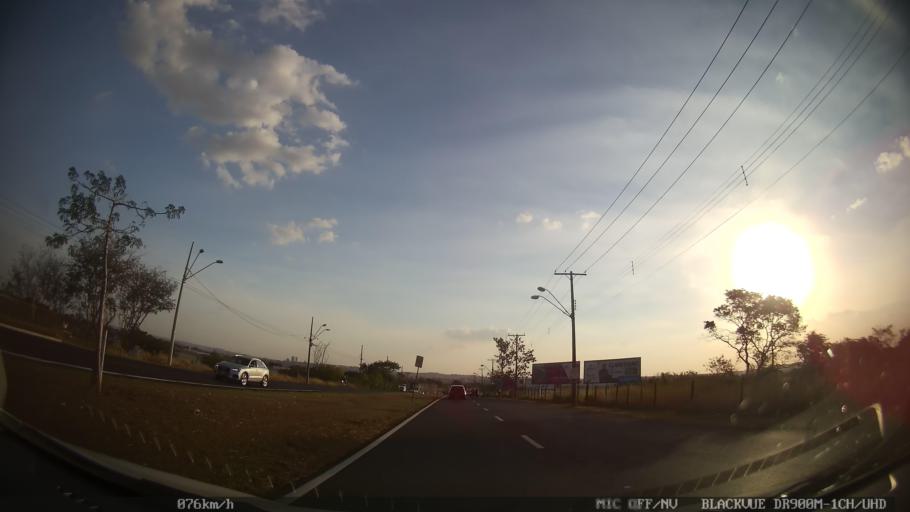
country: BR
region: Sao Paulo
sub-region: Ribeirao Preto
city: Ribeirao Preto
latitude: -21.1297
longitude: -47.7902
